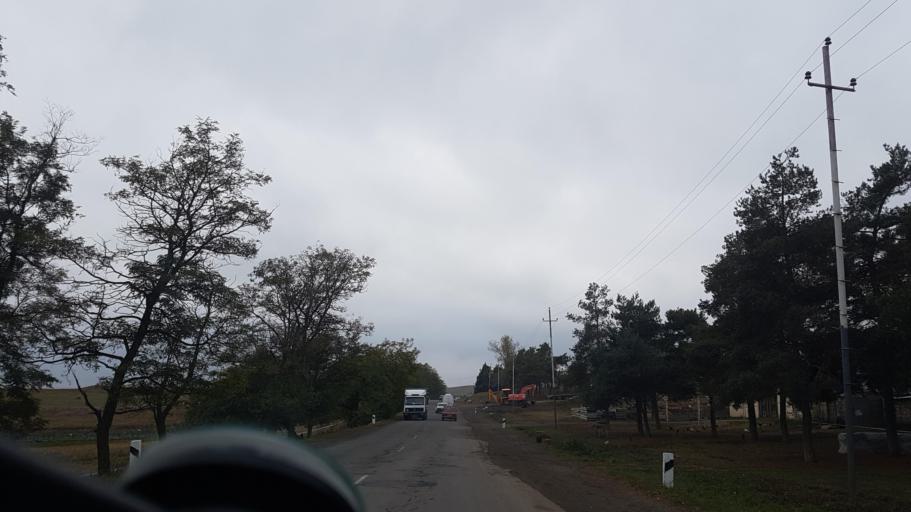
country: AZ
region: Gadabay Rayon
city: Ariqdam
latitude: 40.6414
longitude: 45.8128
